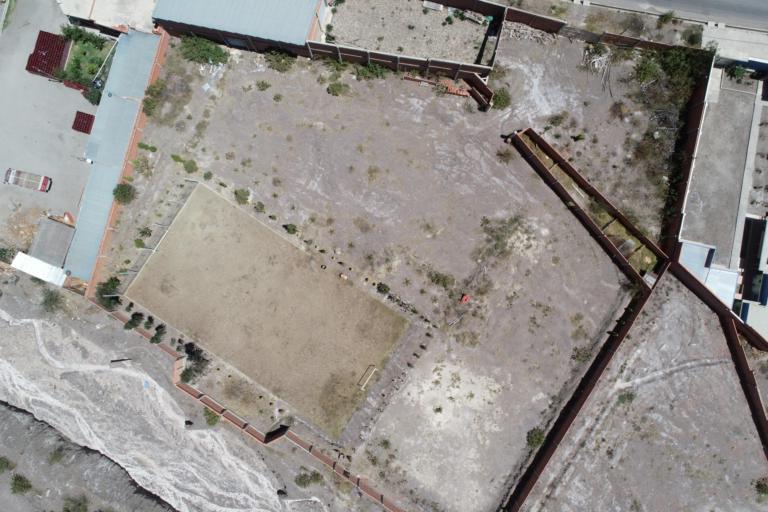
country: BO
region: La Paz
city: La Paz
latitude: -16.6422
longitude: -68.0412
